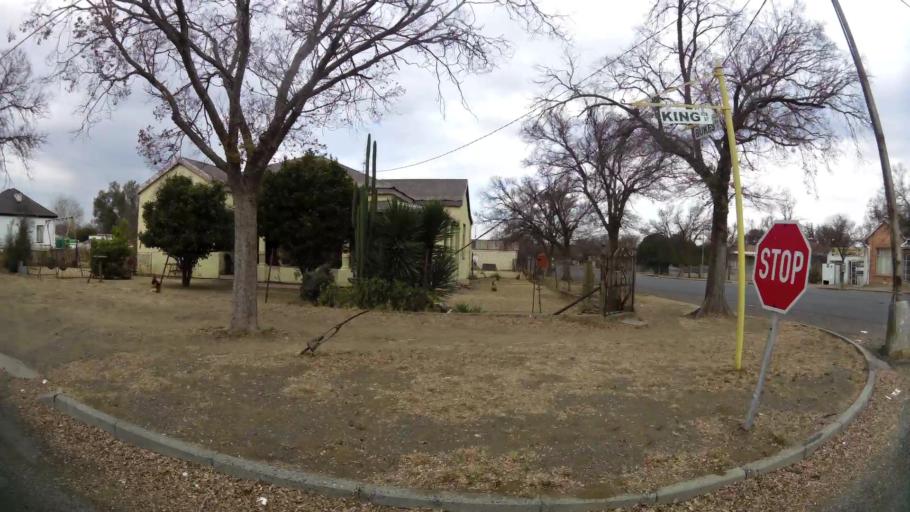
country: ZA
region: Orange Free State
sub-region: Fezile Dabi District Municipality
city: Kroonstad
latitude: -27.6557
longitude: 27.2424
